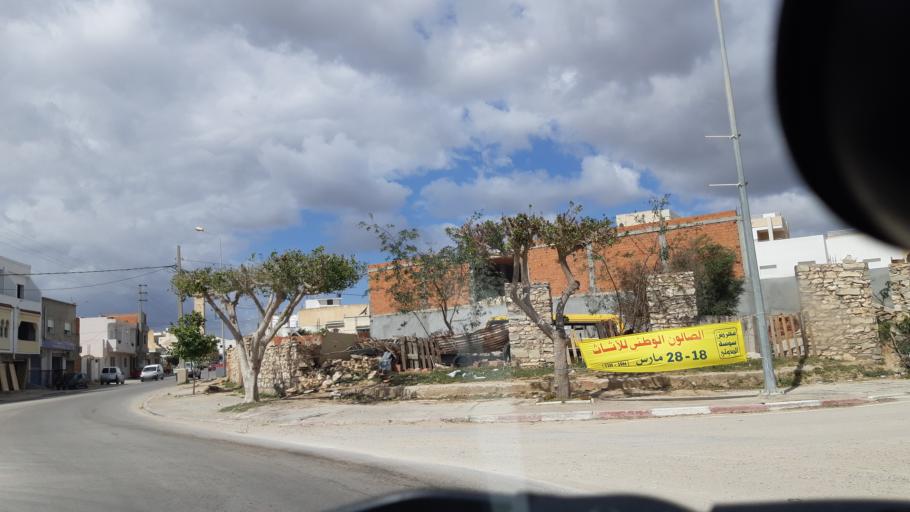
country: TN
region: Susah
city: Akouda
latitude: 35.8724
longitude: 10.5489
